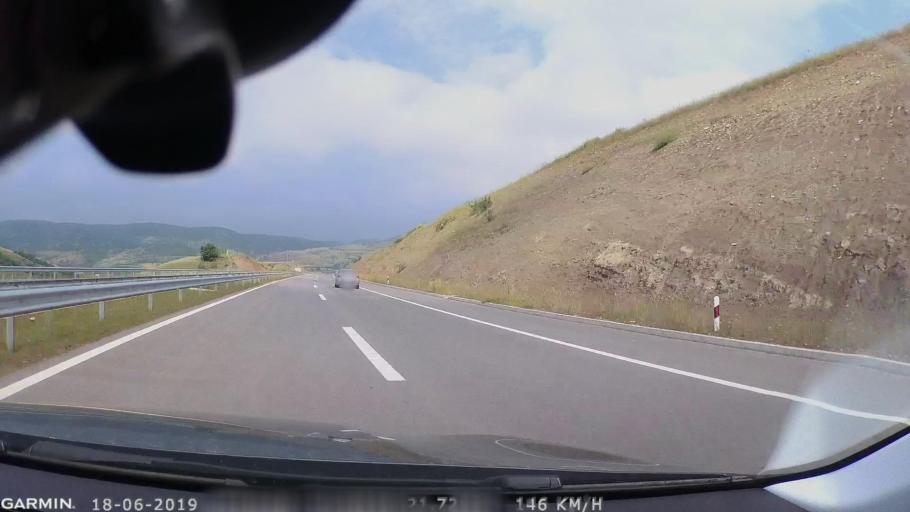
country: MK
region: Sveti Nikole
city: Gorobinci
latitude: 41.9308
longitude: 21.8279
